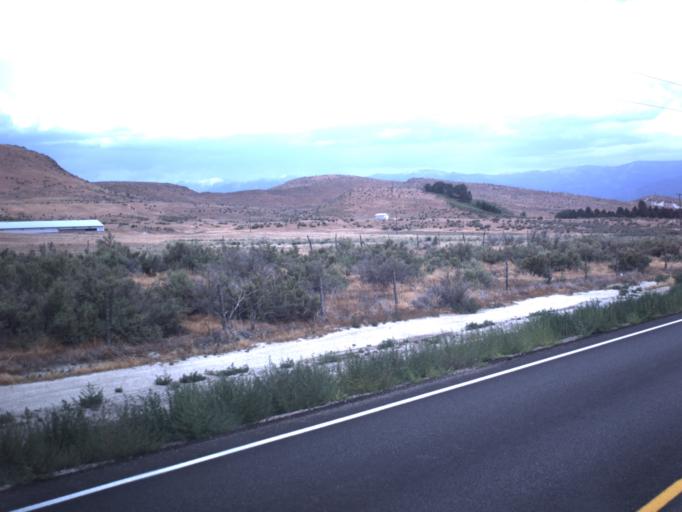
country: US
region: Utah
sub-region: Sanpete County
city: Moroni
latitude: 39.5470
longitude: -111.5981
